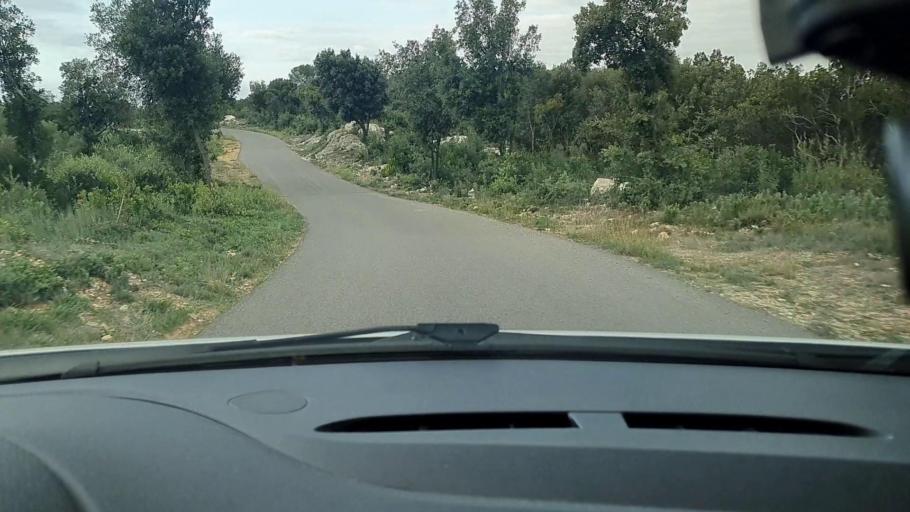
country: FR
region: Languedoc-Roussillon
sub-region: Departement du Gard
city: Mons
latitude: 44.1417
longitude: 4.2645
